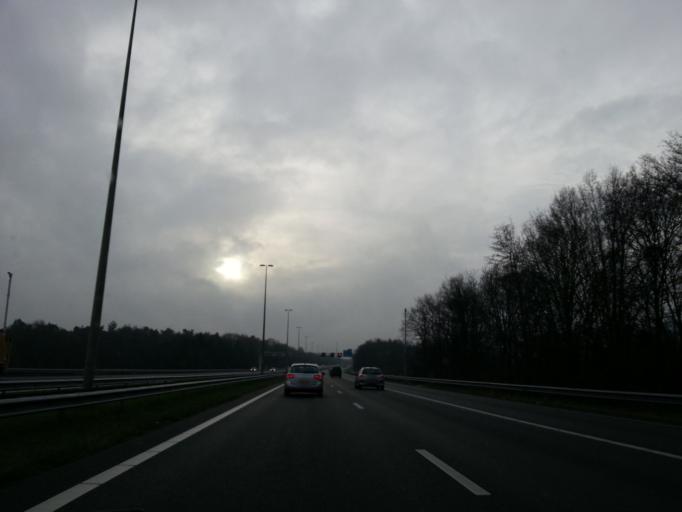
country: NL
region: Gelderland
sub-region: Gemeente Apeldoorn
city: Loenen
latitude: 52.1552
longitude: 6.0147
